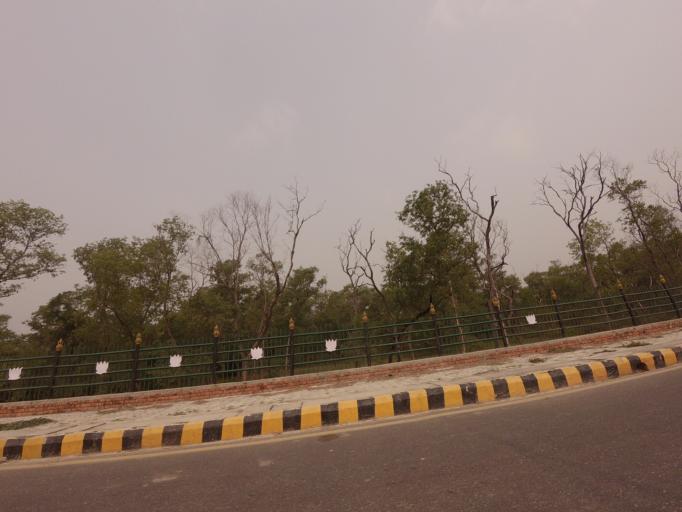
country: IN
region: Uttar Pradesh
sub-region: Maharajganj
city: Nautanwa
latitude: 27.4814
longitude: 83.2840
